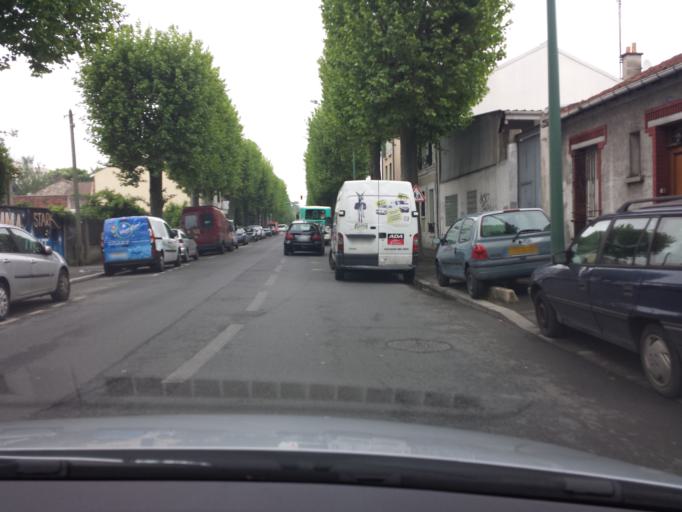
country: FR
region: Ile-de-France
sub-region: Departement du Val-de-Marne
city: Arcueil
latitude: 48.8027
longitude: 2.3343
